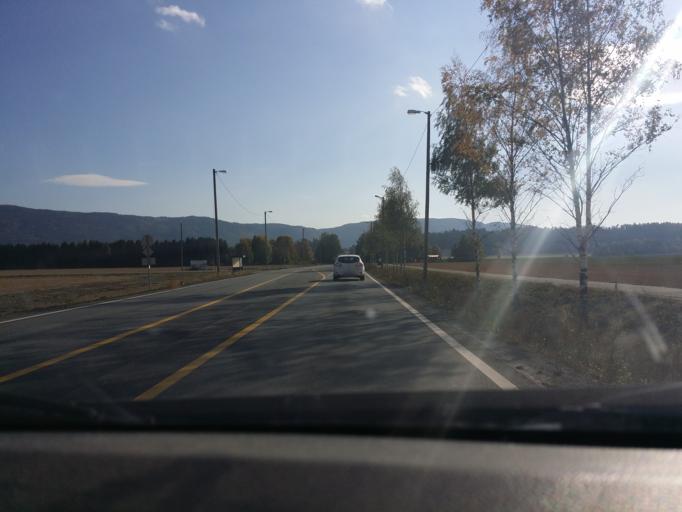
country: NO
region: Buskerud
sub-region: Hole
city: Vik
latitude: 60.1110
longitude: 10.2851
